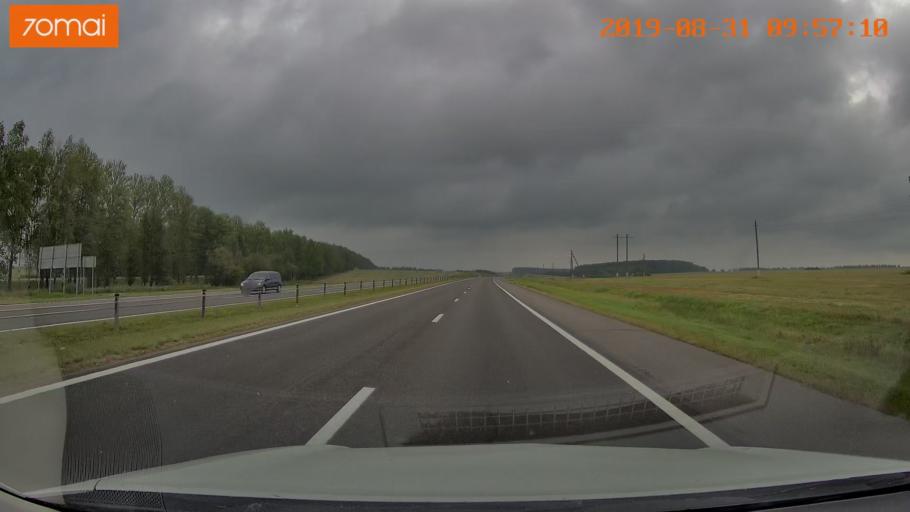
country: BY
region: Mogilev
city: Vishow
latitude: 53.9811
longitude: 29.9201
